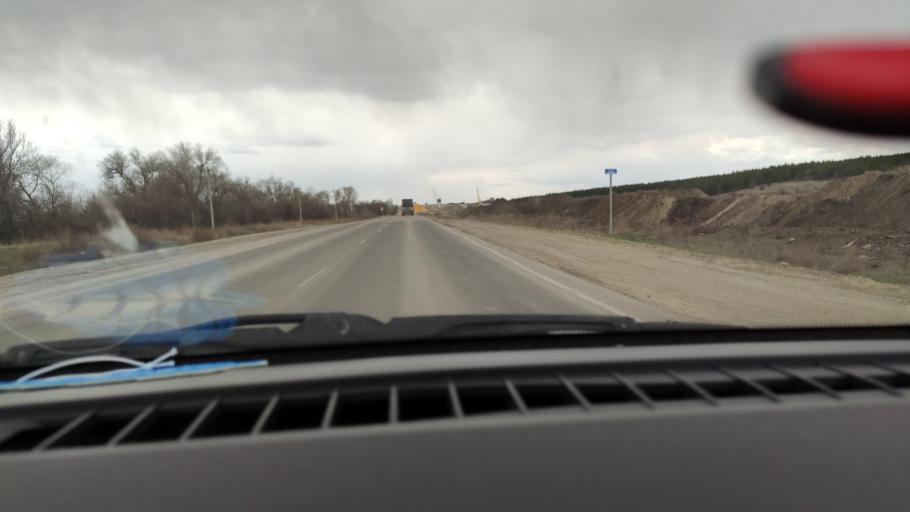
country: RU
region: Saratov
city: Sinodskoye
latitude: 52.0146
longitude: 46.6958
